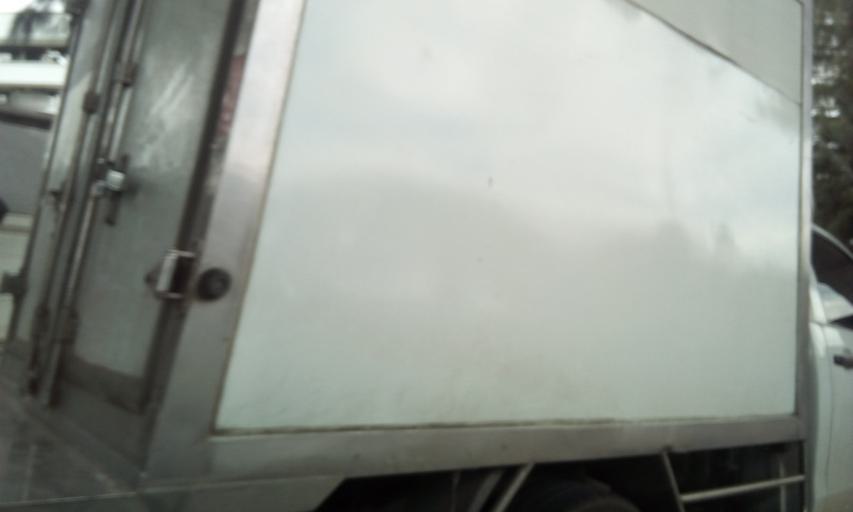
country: TH
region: Bangkok
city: Lak Si
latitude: 13.8785
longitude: 100.5776
